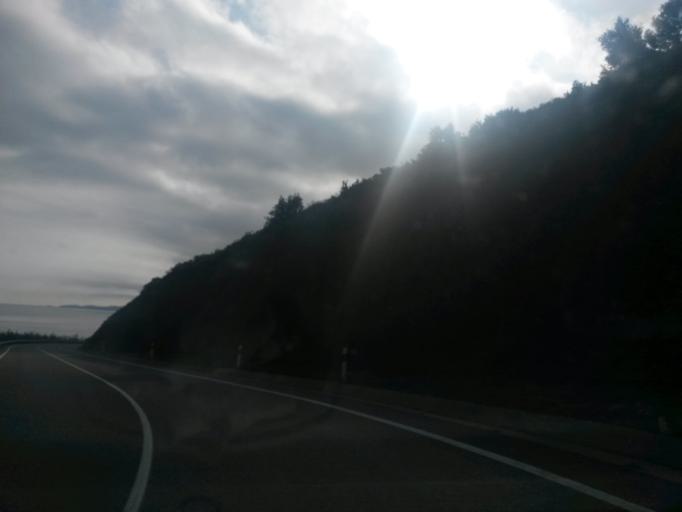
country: ES
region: Catalonia
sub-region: Provincia de Girona
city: Colera
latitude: 42.4122
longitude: 3.1539
